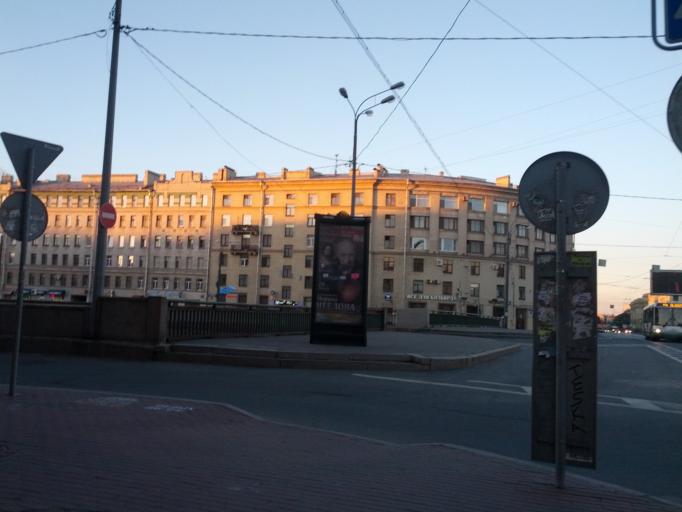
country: RU
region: St.-Petersburg
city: Saint Petersburg
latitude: 59.9092
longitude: 30.3186
